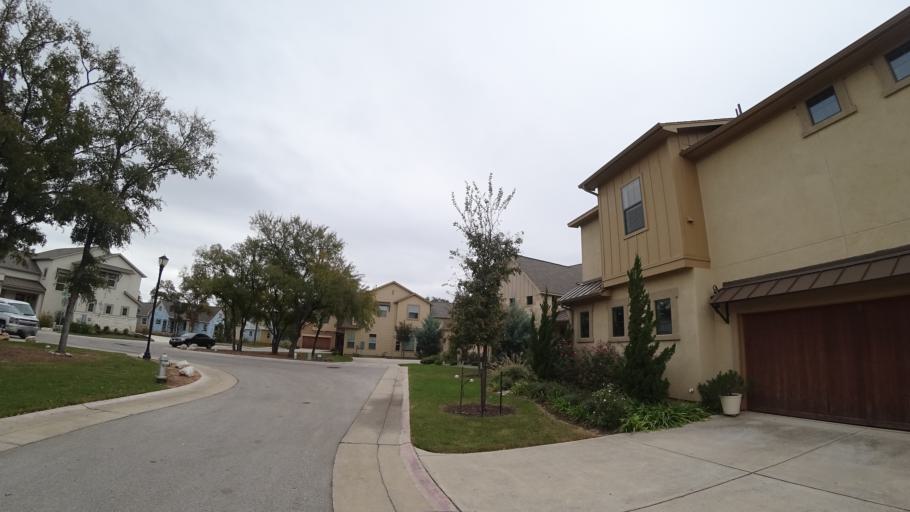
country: US
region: Texas
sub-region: Travis County
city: Shady Hollow
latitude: 30.1485
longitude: -97.8538
